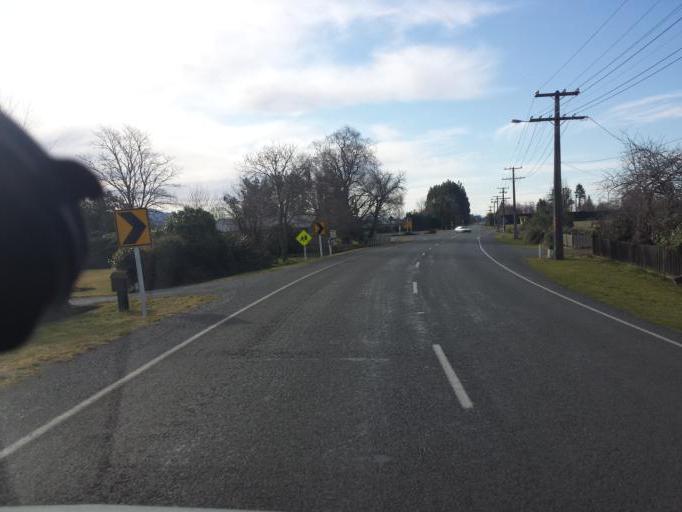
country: NZ
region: Canterbury
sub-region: Timaru District
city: Pleasant Point
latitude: -44.0718
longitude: 171.2480
